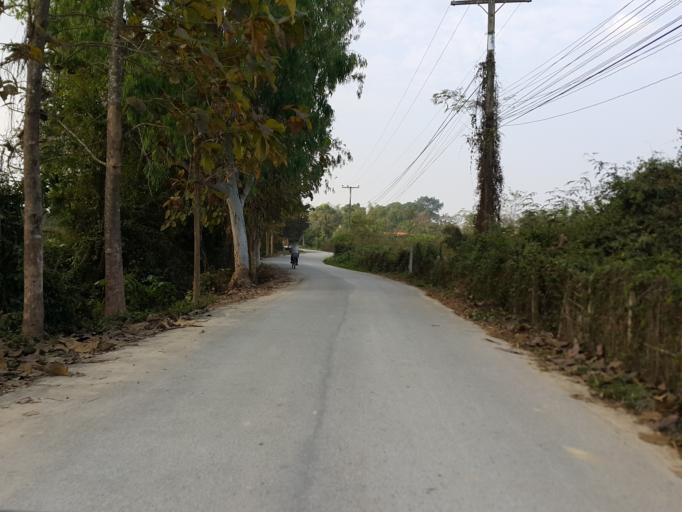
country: TH
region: Chiang Mai
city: San Sai
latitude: 18.8262
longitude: 99.0914
